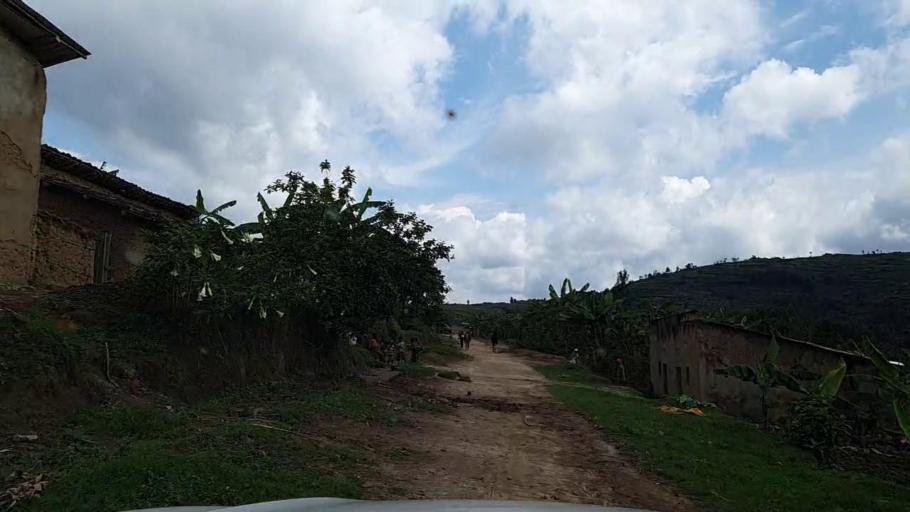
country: RW
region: Southern Province
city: Gikongoro
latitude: -2.3947
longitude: 29.5525
